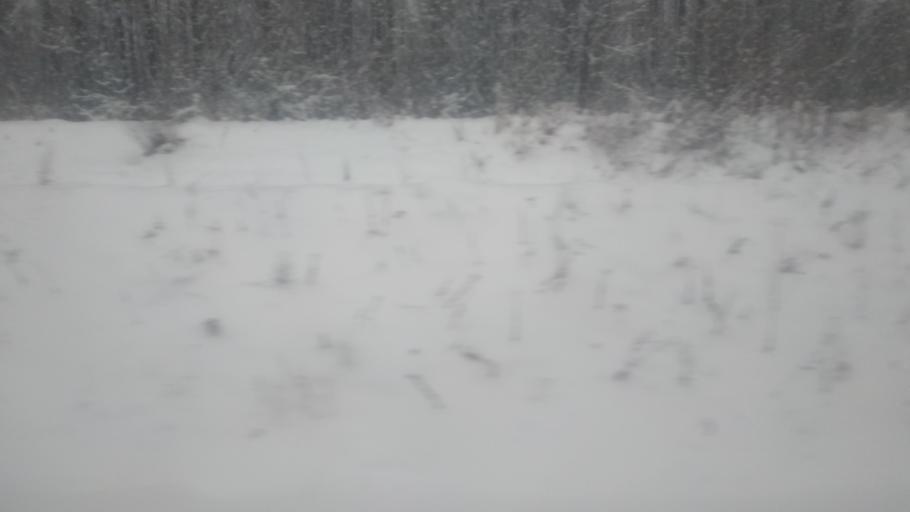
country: RU
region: Bashkortostan
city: Amzya
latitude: 56.2326
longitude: 54.4839
